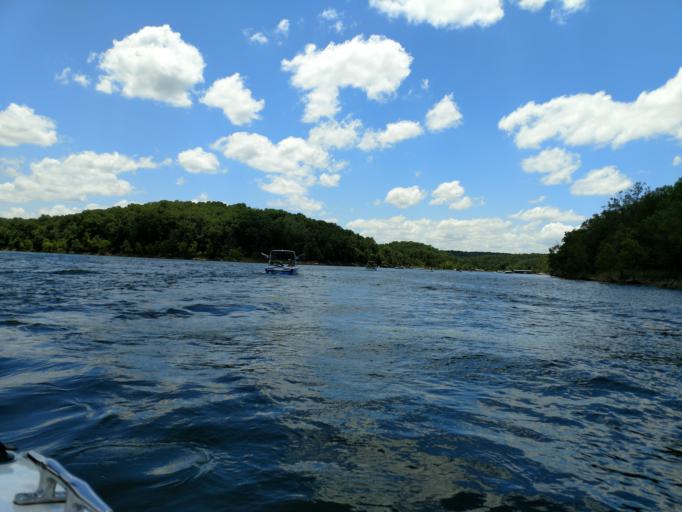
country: US
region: Missouri
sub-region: Barry County
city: Shell Knob
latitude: 36.5750
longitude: -93.5648
